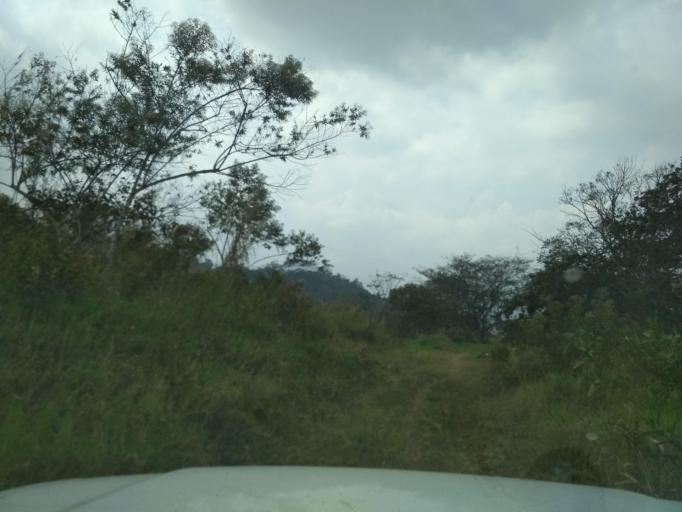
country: MX
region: Veracruz
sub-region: Cordoba
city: San Jose de Tapia
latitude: 18.8338
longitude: -96.9741
